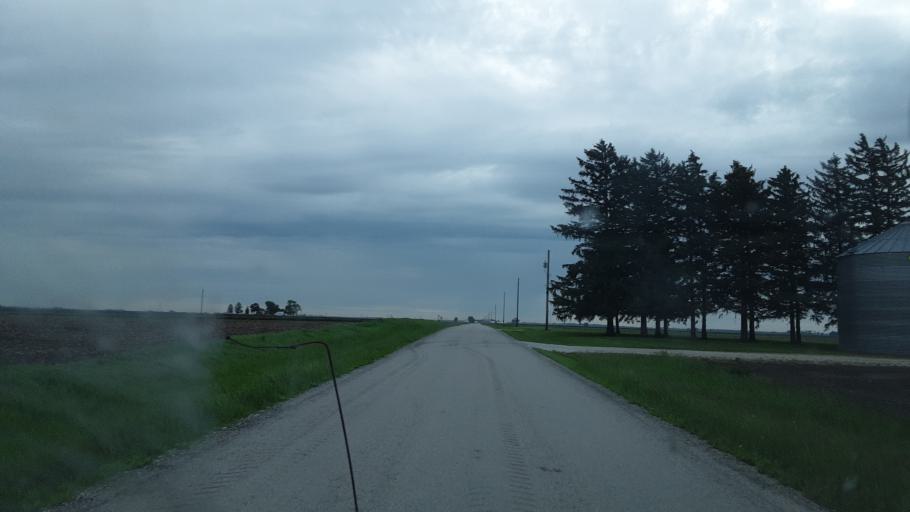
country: US
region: Illinois
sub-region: McDonough County
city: Macomb
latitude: 40.3819
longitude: -90.5570
